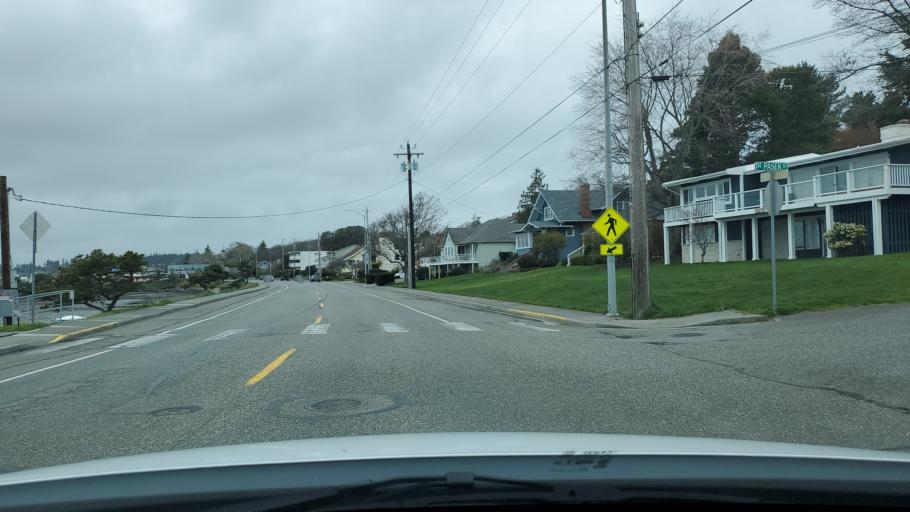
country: US
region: Washington
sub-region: Island County
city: Oak Harbor
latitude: 48.2898
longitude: -122.6384
